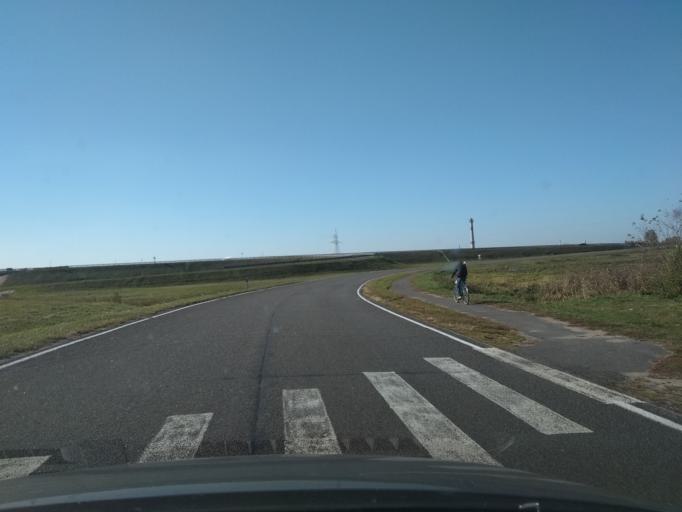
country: BY
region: Brest
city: Ivatsevichy
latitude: 52.7012
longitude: 25.3657
